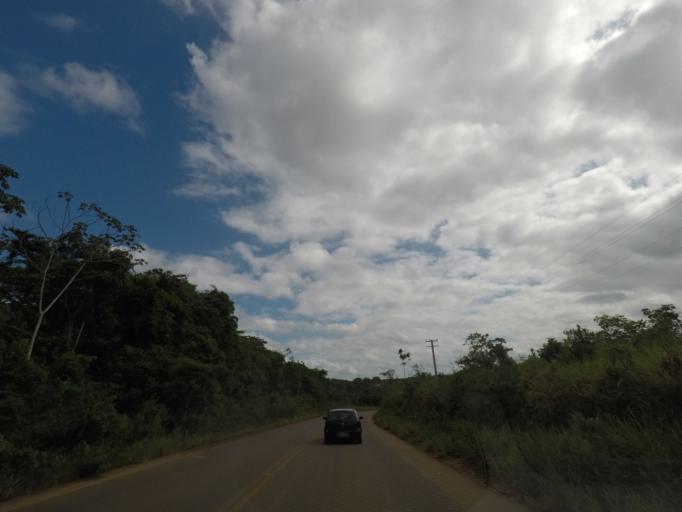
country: BR
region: Bahia
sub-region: Itacare
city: Itacare
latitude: -14.2089
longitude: -39.1007
